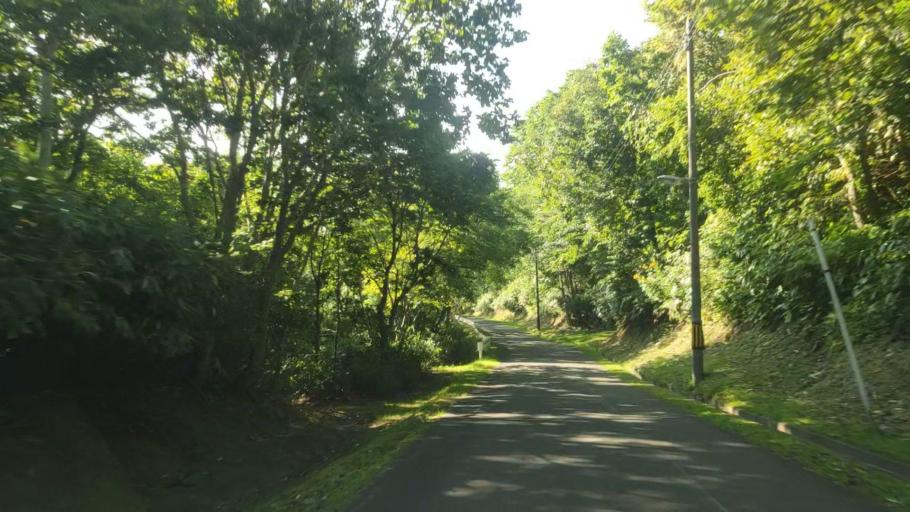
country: JP
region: Hokkaido
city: Wakkanai
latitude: 45.4151
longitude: 141.6672
